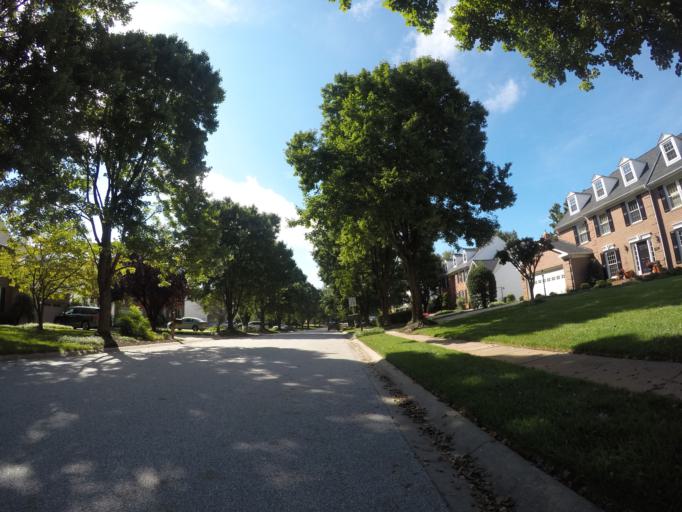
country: US
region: Maryland
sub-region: Howard County
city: Columbia
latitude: 39.2661
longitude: -76.8671
